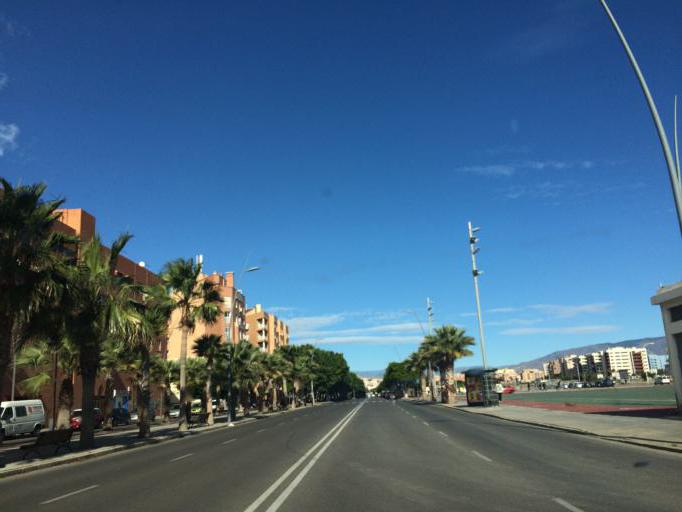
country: ES
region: Andalusia
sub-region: Provincia de Almeria
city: Almeria
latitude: 36.8247
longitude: -2.4450
